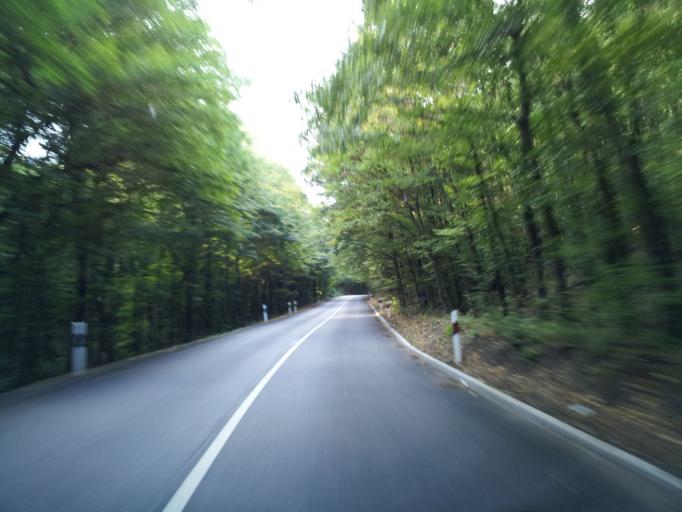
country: HU
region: Pest
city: Nagymaros
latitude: 47.8356
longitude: 18.9586
